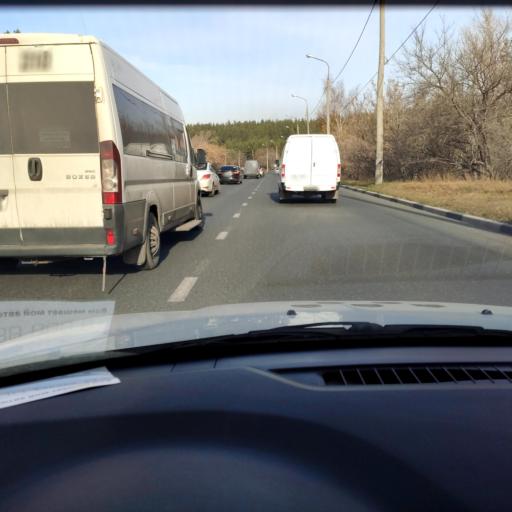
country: RU
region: Samara
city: Zhigulevsk
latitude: 53.4996
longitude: 49.4726
